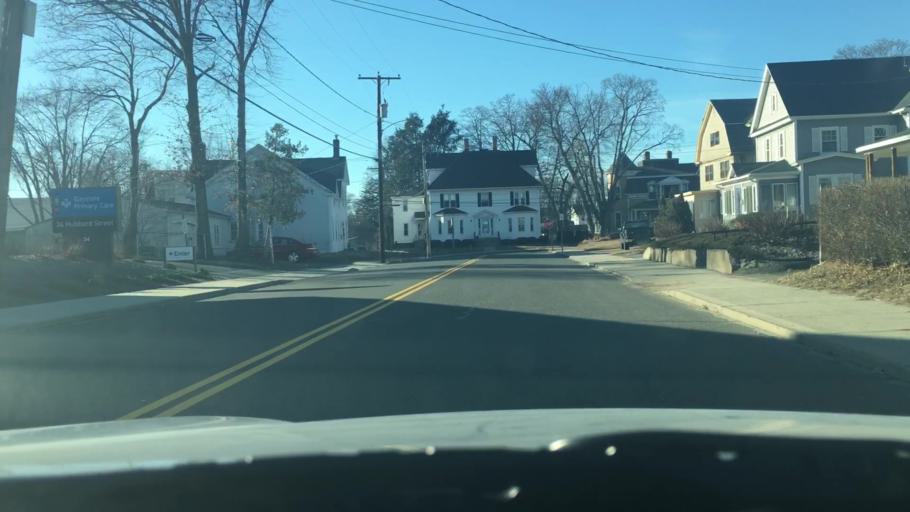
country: US
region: Massachusetts
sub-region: Hampden County
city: Ludlow
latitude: 42.1606
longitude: -72.4831
